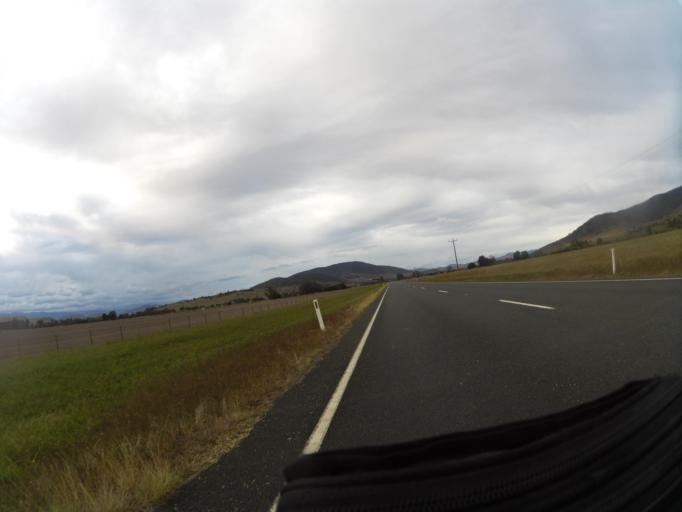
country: AU
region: New South Wales
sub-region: Snowy River
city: Jindabyne
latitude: -36.1066
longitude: 147.9801
